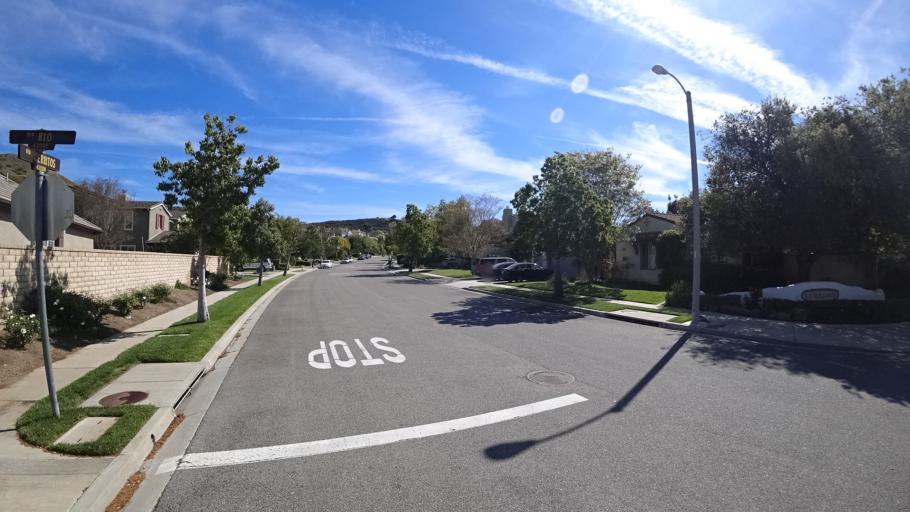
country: US
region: California
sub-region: Ventura County
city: Casa Conejo
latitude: 34.1721
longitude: -118.9685
